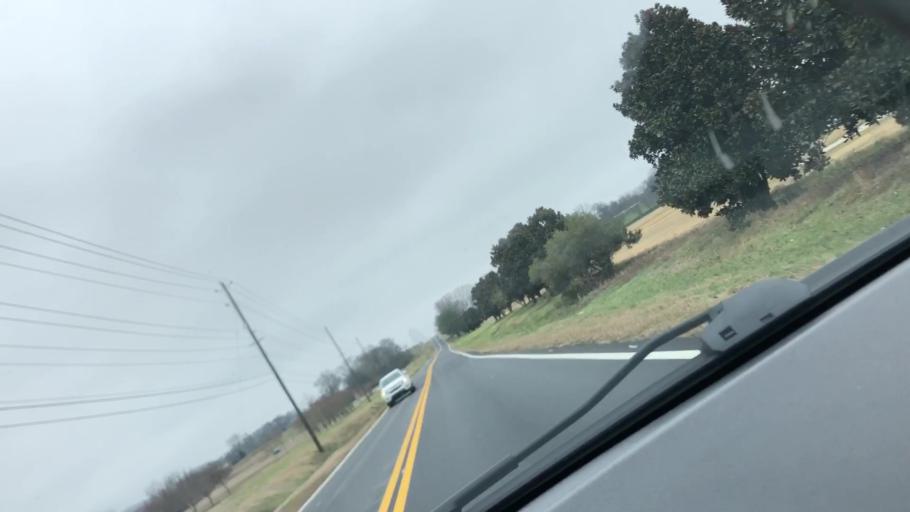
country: US
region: Georgia
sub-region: Bartow County
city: Cartersville
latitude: 34.1217
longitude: -84.8206
